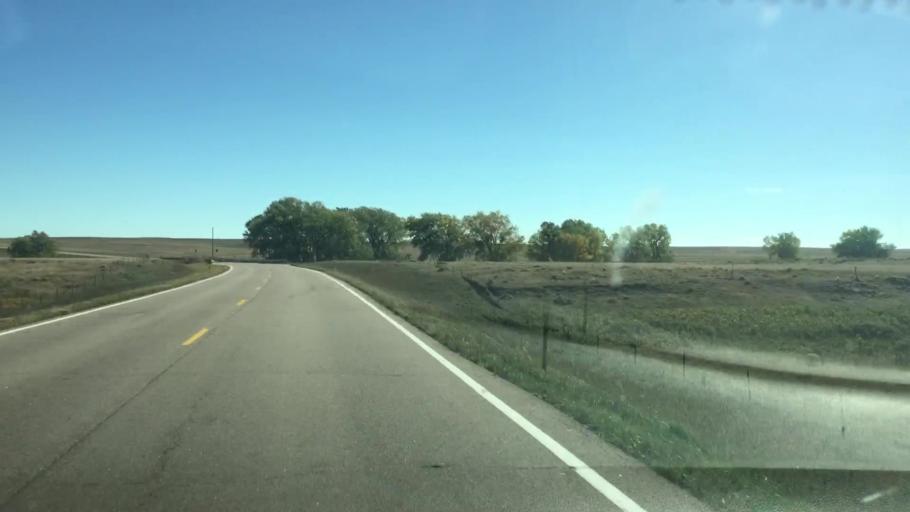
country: US
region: Colorado
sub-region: Lincoln County
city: Limon
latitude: 39.2735
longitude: -104.0118
